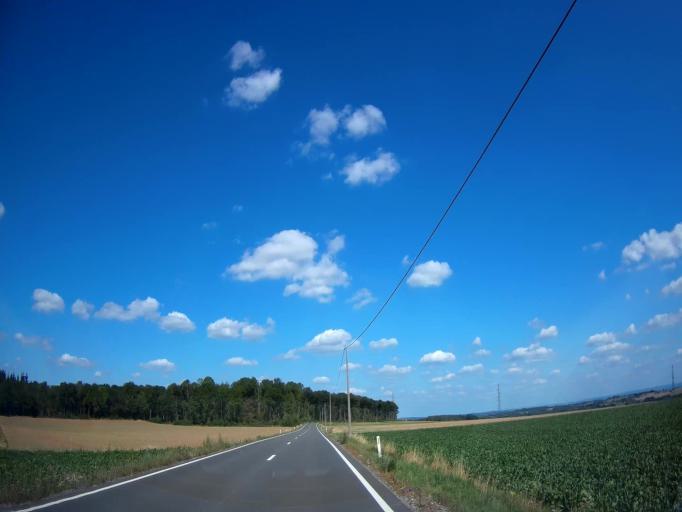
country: FR
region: Champagne-Ardenne
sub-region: Departement des Ardennes
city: Fromelennes
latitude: 50.1742
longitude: 4.9072
